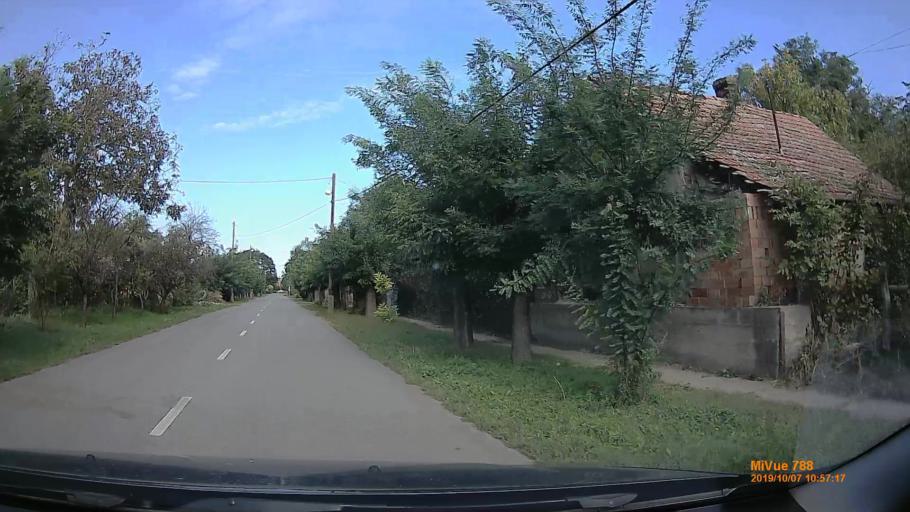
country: HU
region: Bekes
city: Kondoros
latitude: 46.7535
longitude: 20.7990
